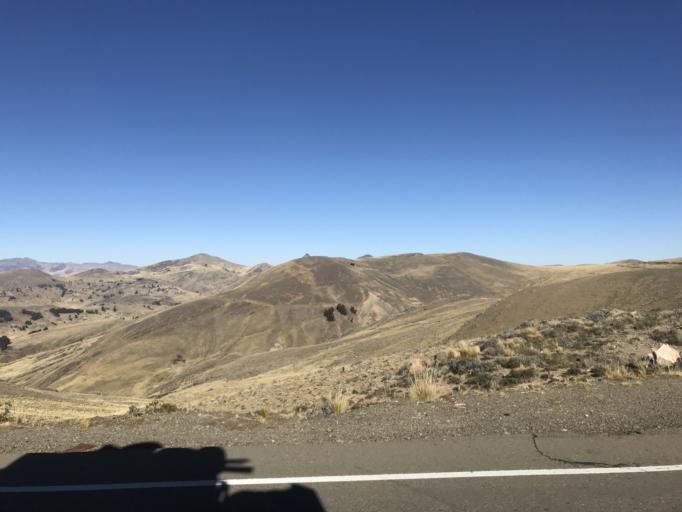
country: PE
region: Puno
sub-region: Yunguyo
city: Yunguyo
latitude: -16.1563
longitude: -68.9947
